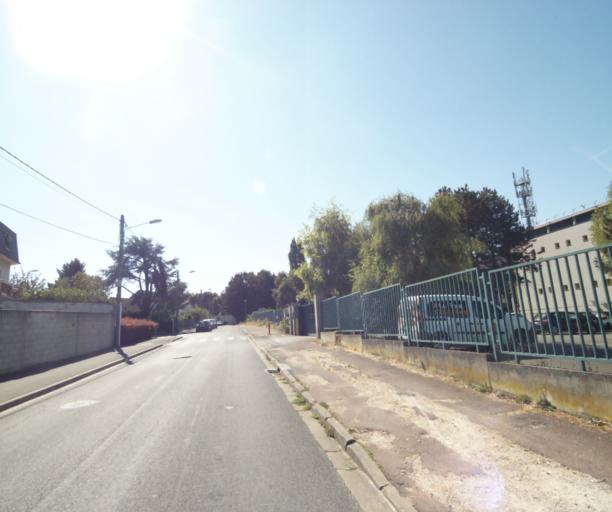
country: FR
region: Ile-de-France
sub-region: Departement de Seine-et-Marne
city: Lagny-sur-Marne
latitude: 48.8695
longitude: 2.7085
